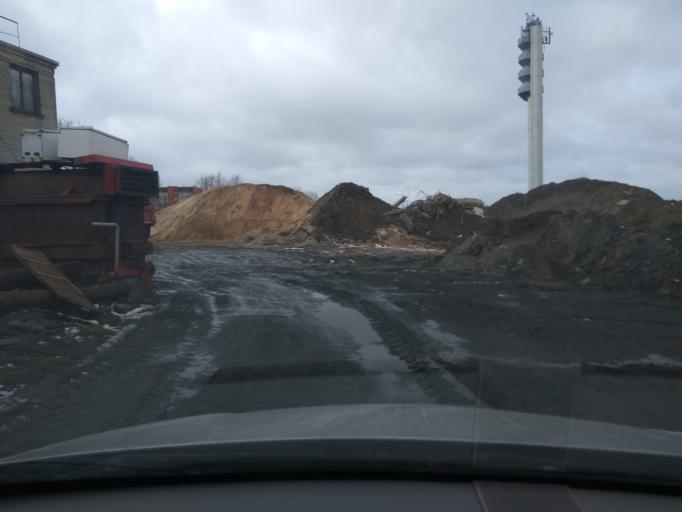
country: LV
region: Ventspils
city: Ventspils
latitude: 57.3330
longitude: 21.6398
